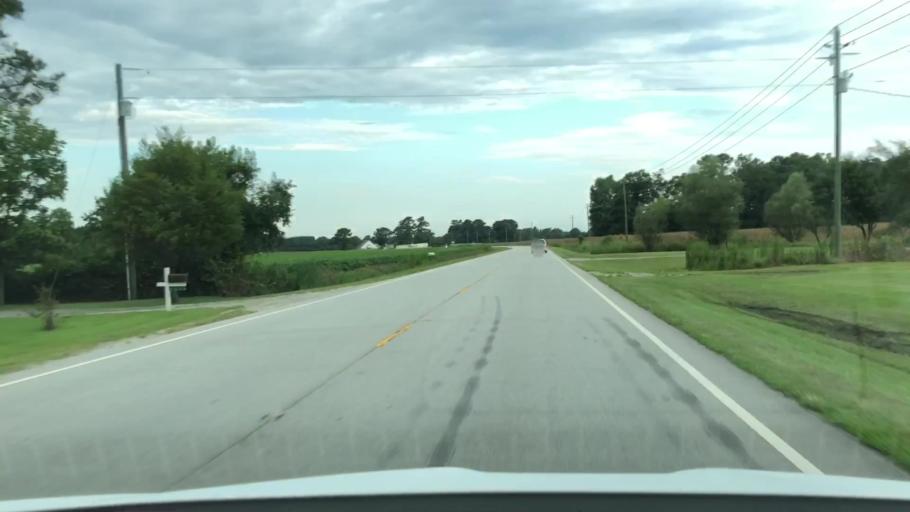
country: US
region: North Carolina
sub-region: Jones County
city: Trenton
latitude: 35.0769
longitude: -77.3941
